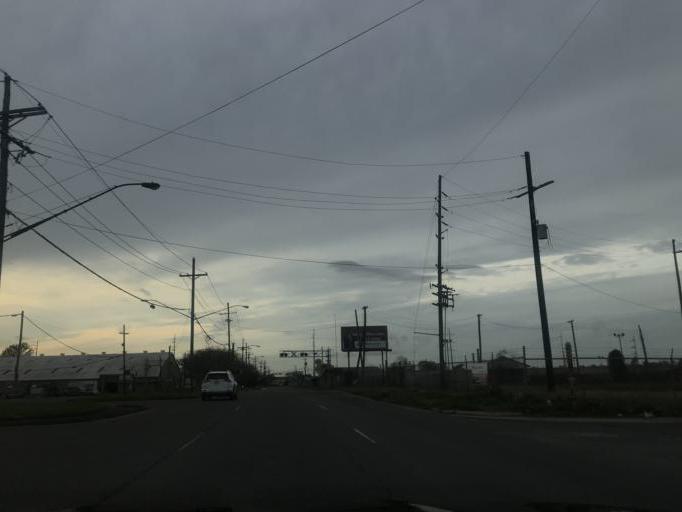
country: US
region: Louisiana
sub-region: Jefferson Parish
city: Jefferson
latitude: 29.9649
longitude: -90.1333
